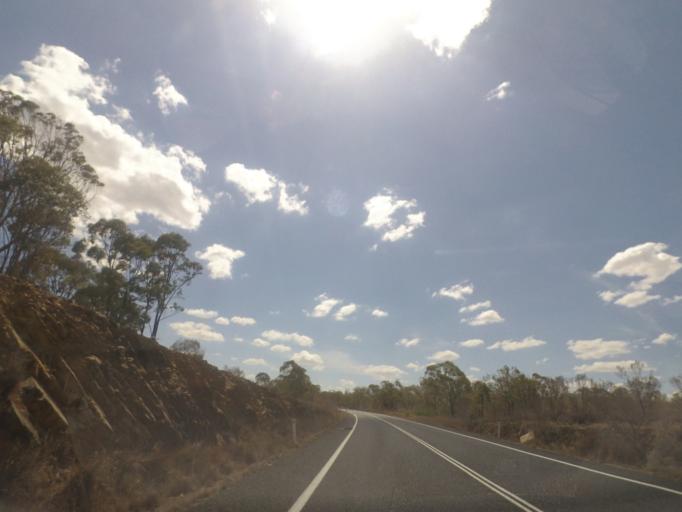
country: AU
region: Queensland
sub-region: Southern Downs
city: Warwick
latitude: -28.1614
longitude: 151.6946
